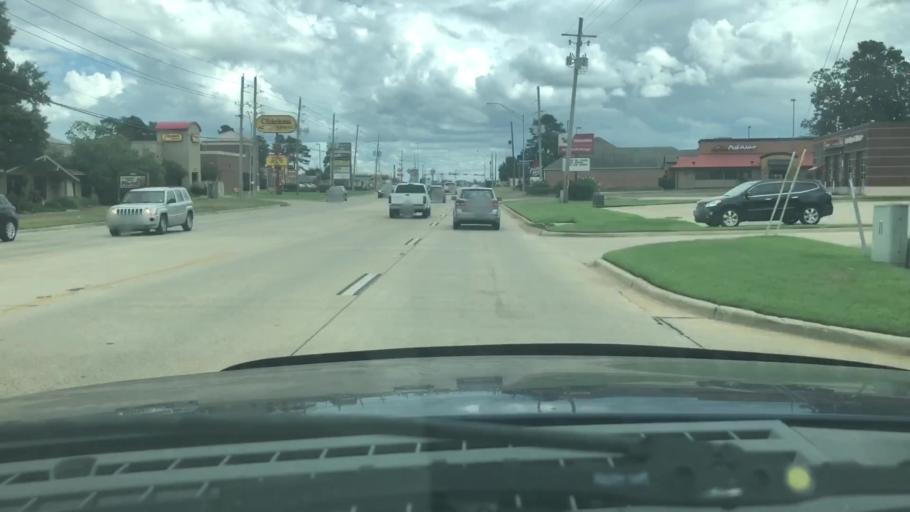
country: US
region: Texas
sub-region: Bowie County
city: Wake Village
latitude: 33.4627
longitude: -94.0931
